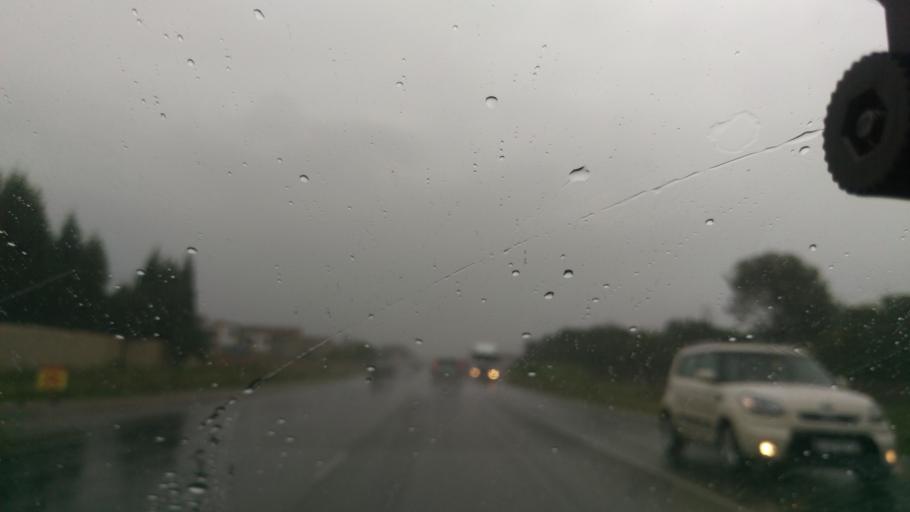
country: ZA
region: Gauteng
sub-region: City of Johannesburg Metropolitan Municipality
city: Diepsloot
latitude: -26.0364
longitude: 27.9618
